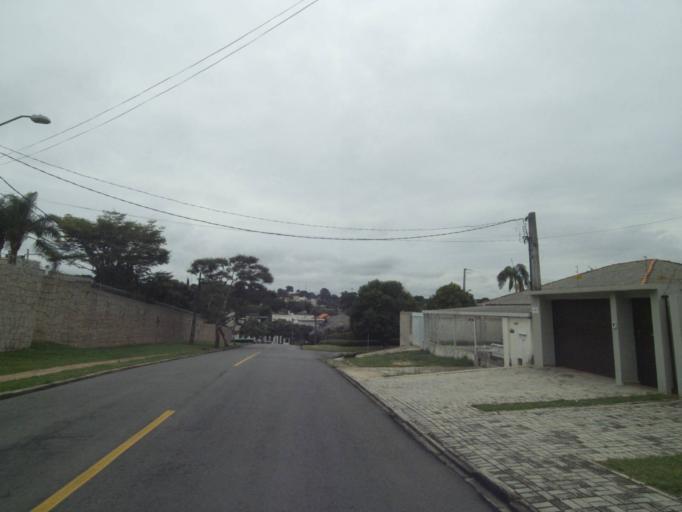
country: BR
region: Parana
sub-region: Curitiba
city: Curitiba
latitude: -25.4094
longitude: -49.2842
